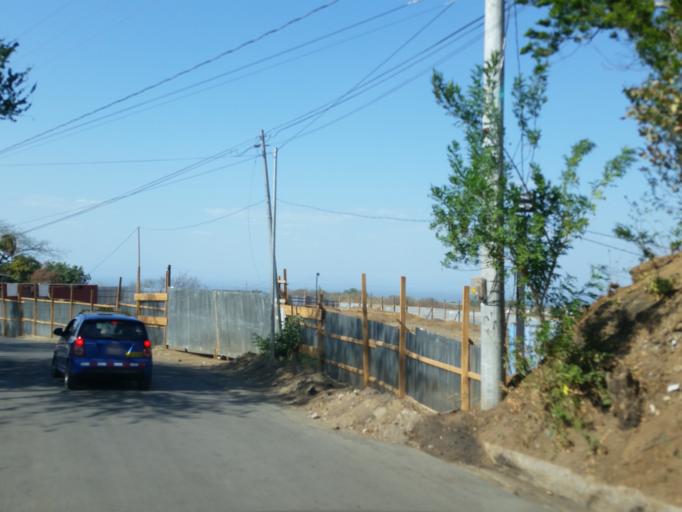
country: NI
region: Managua
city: Managua
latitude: 12.0985
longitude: -86.2910
